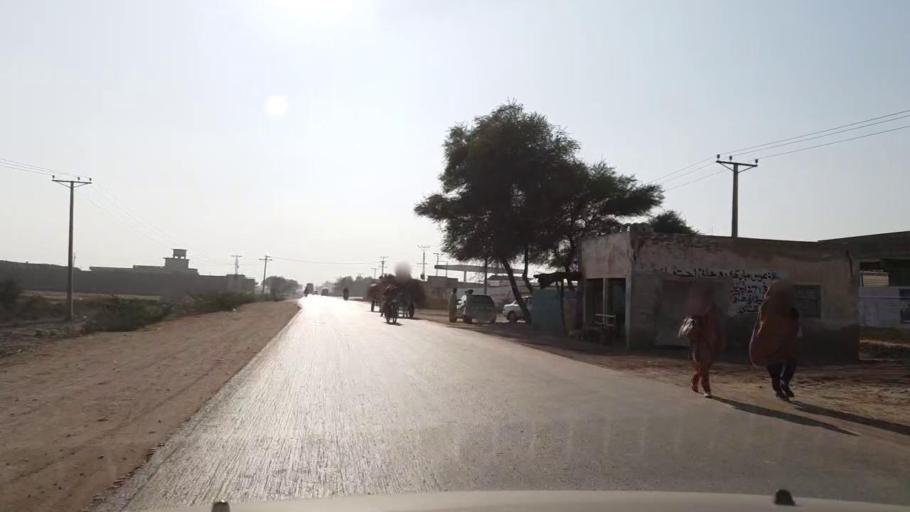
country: PK
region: Sindh
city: Tando Muhammad Khan
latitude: 25.1120
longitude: 68.5239
